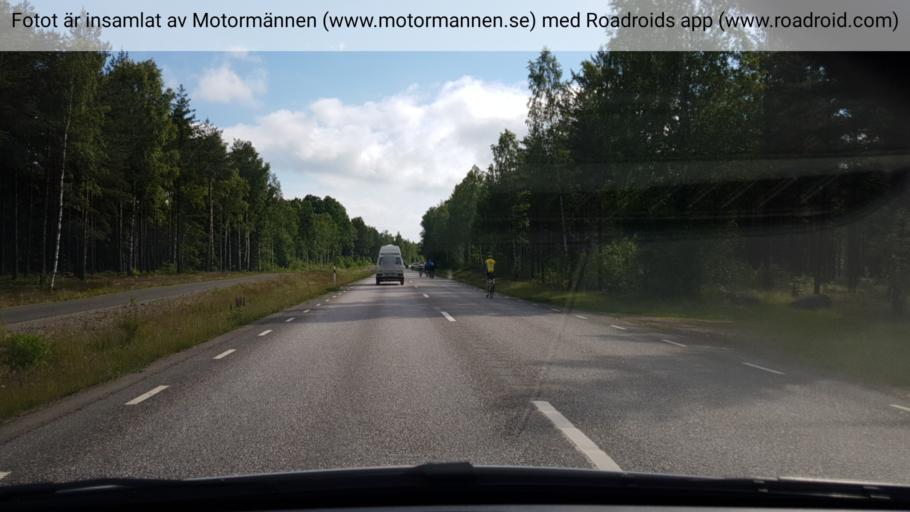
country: SE
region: Vaestra Goetaland
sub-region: Karlsborgs Kommun
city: Karlsborg
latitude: 58.5154
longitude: 14.4845
